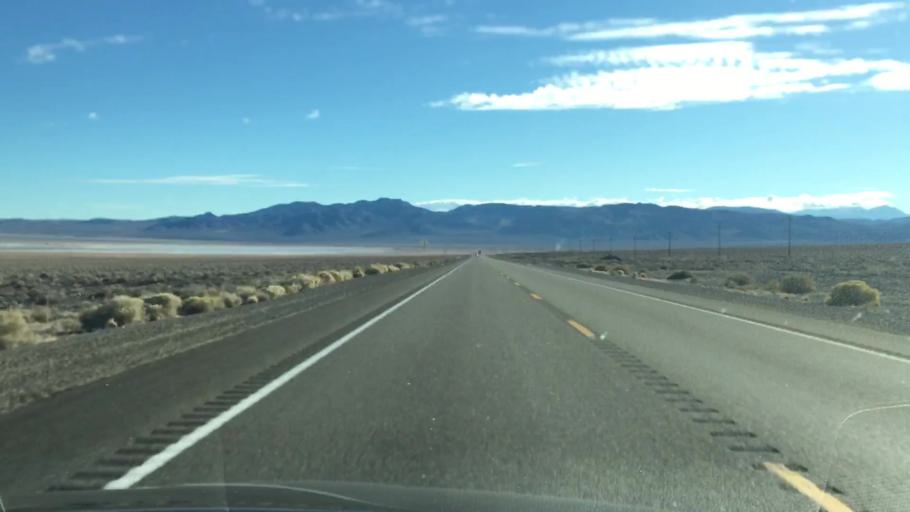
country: US
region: Nevada
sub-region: Mineral County
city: Hawthorne
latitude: 38.3237
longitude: -118.1027
